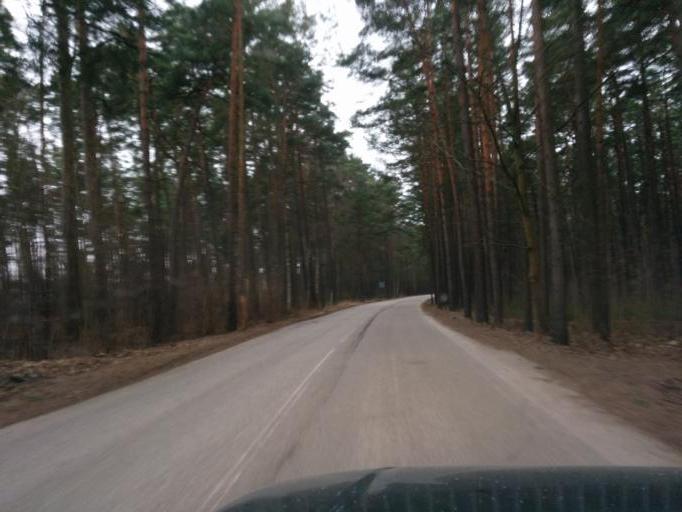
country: LV
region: Babite
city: Pinki
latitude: 56.9918
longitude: 23.9128
